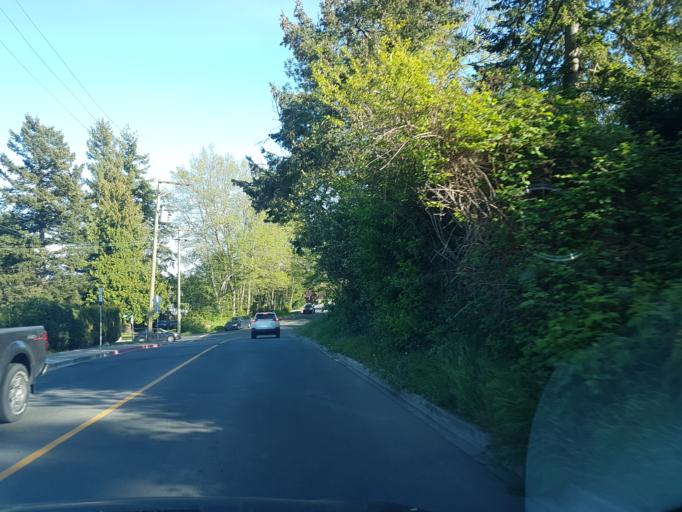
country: CA
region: British Columbia
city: Oak Bay
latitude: 48.4755
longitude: -123.3358
